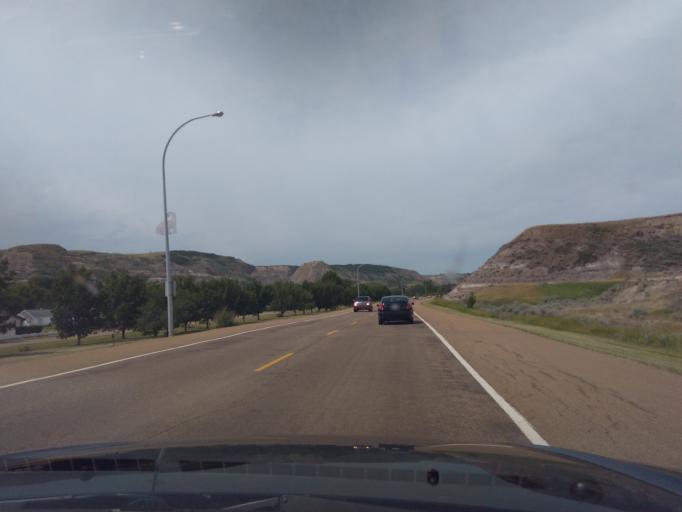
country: CA
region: Alberta
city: Three Hills
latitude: 51.4675
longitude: -112.7529
